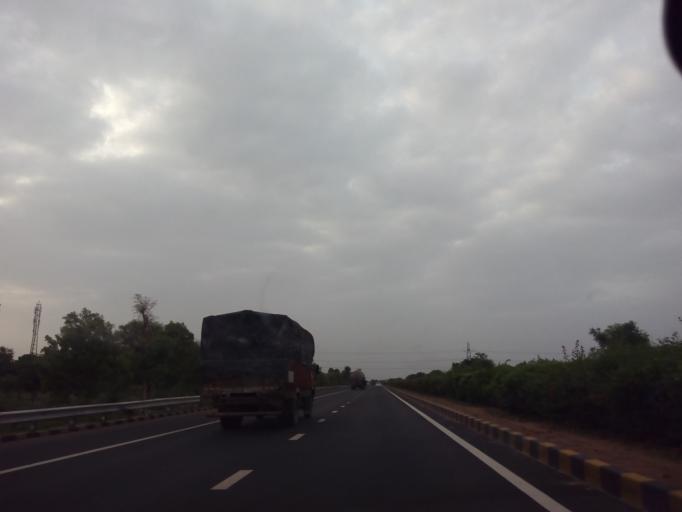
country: IN
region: Gujarat
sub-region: Kheda
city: Mahemdavad
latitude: 22.9369
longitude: 72.7206
